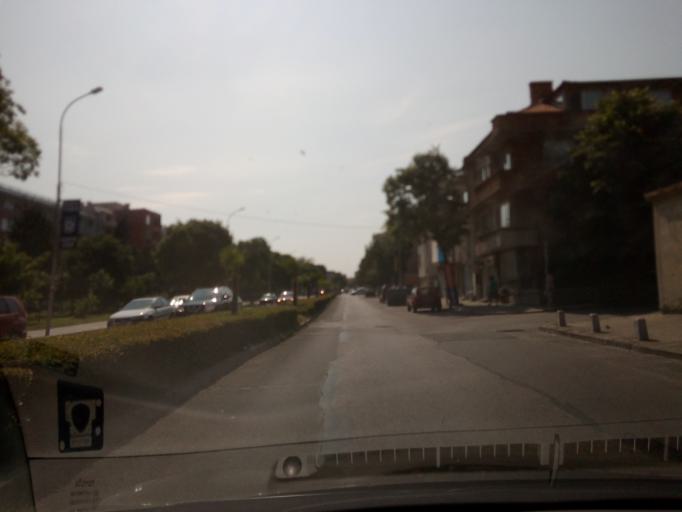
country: BG
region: Burgas
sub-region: Obshtina Pomorie
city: Pomorie
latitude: 42.5616
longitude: 27.6326
